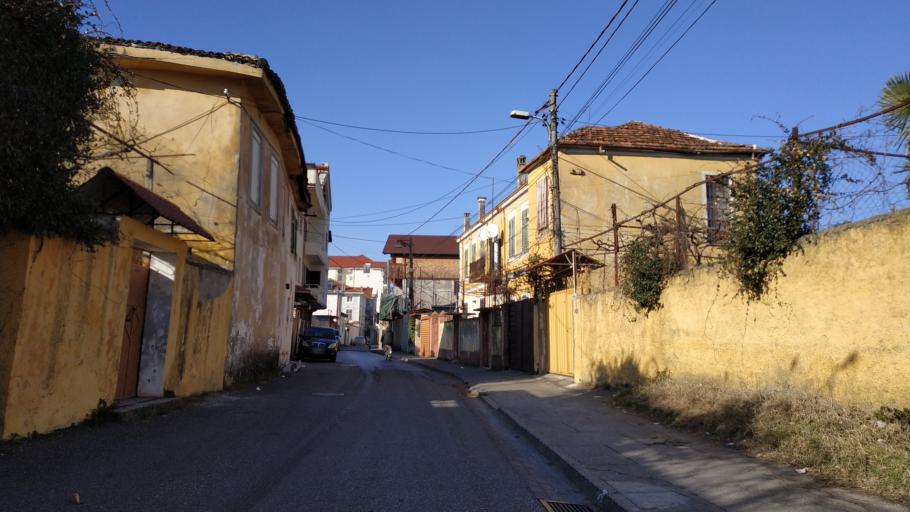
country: AL
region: Shkoder
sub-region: Rrethi i Shkodres
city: Shkoder
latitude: 42.0633
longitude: 19.5203
